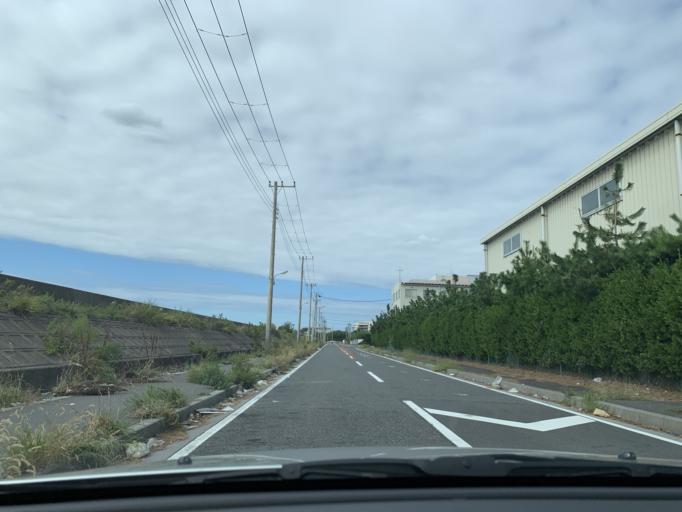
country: JP
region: Tokyo
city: Urayasu
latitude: 35.6199
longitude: 139.8957
